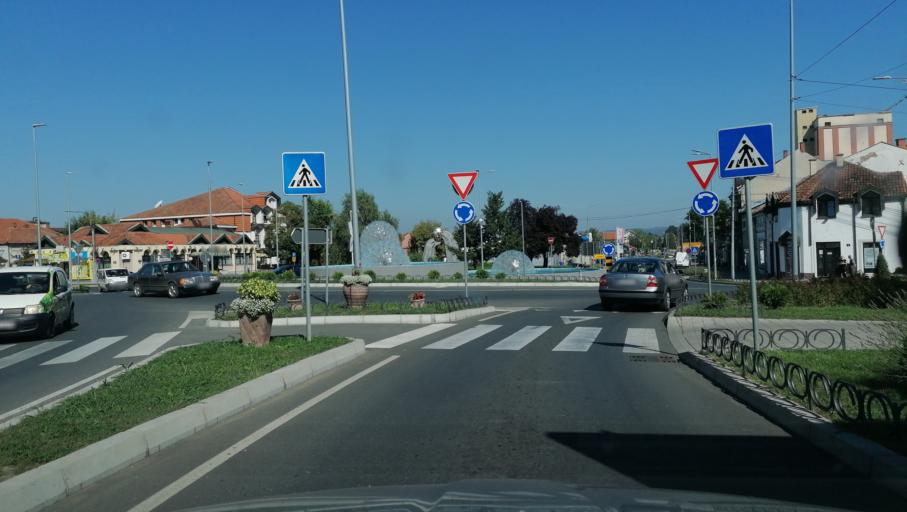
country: RS
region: Central Serbia
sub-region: Rasinski Okrug
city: Krusevac
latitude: 43.5849
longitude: 21.3233
